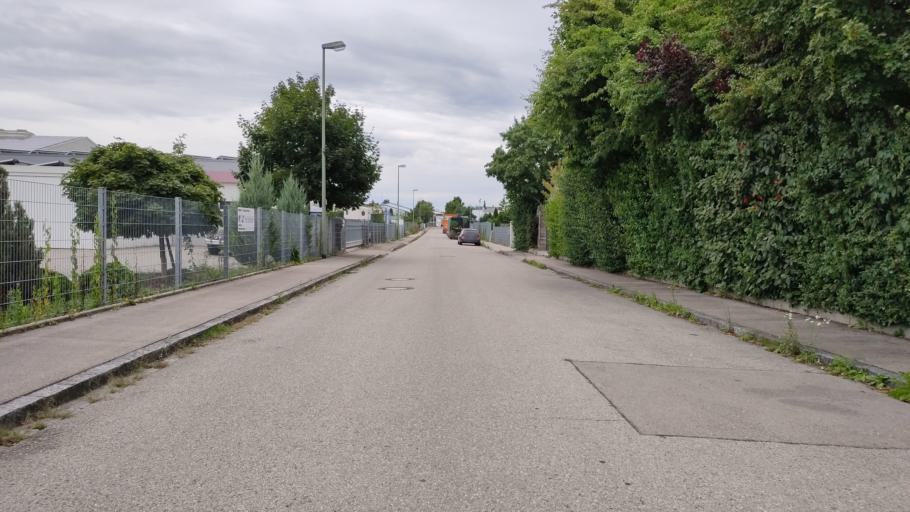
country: DE
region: Bavaria
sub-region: Swabia
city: Oberottmarshausen
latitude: 48.2498
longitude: 10.8741
